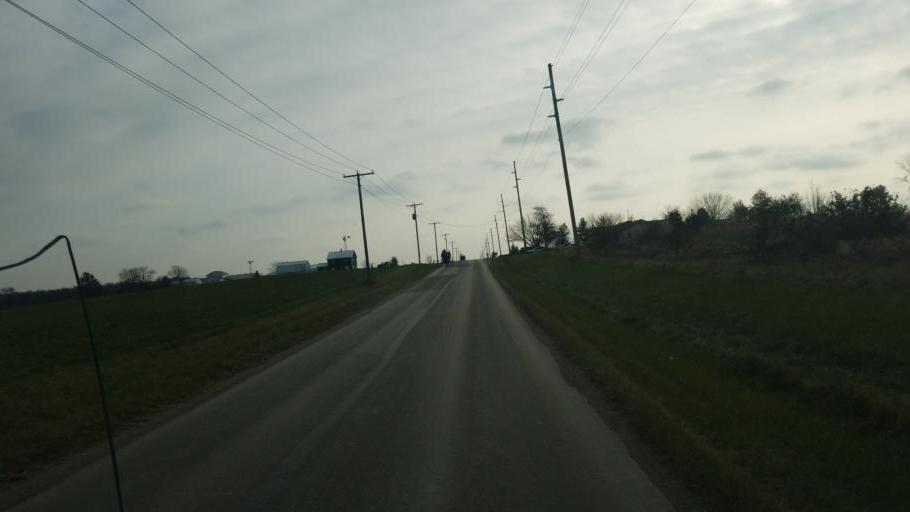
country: US
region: Indiana
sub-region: Adams County
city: Berne
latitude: 40.6373
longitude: -84.9643
